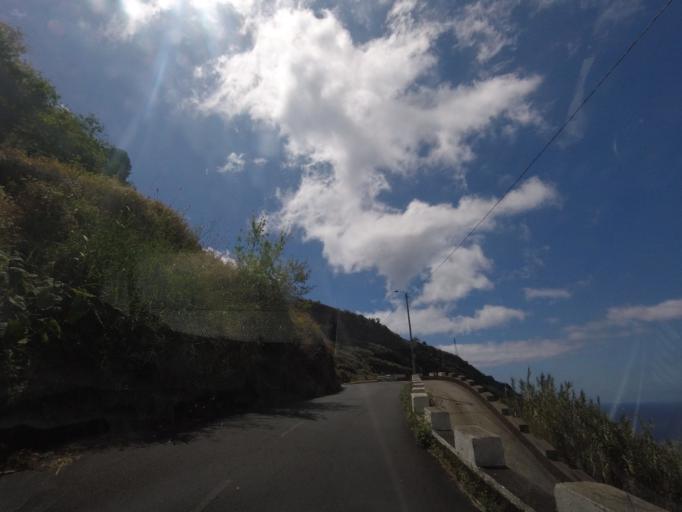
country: PT
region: Madeira
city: Ponta do Sol
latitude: 32.6871
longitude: -17.0828
